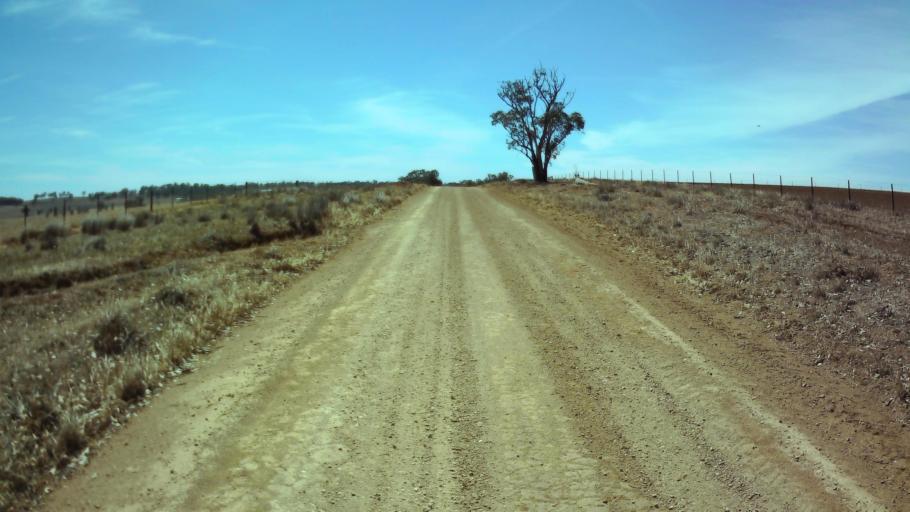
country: AU
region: New South Wales
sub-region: Weddin
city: Grenfell
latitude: -33.9444
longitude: 148.1538
